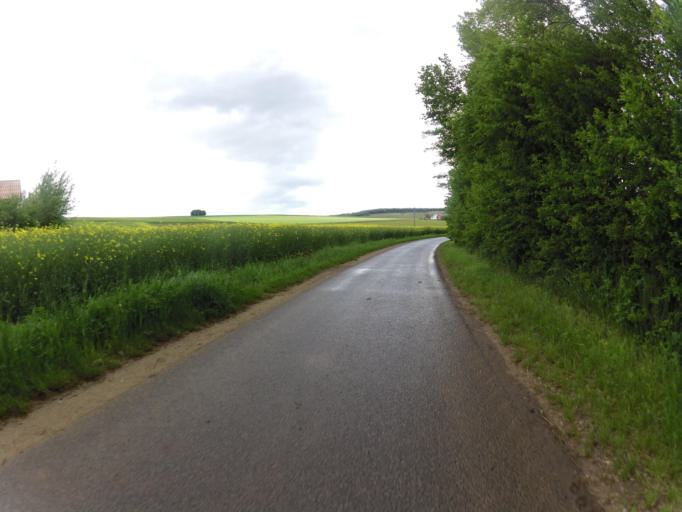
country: DE
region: Bavaria
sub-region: Regierungsbezirk Unterfranken
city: Volkach
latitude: 49.8711
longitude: 10.2472
